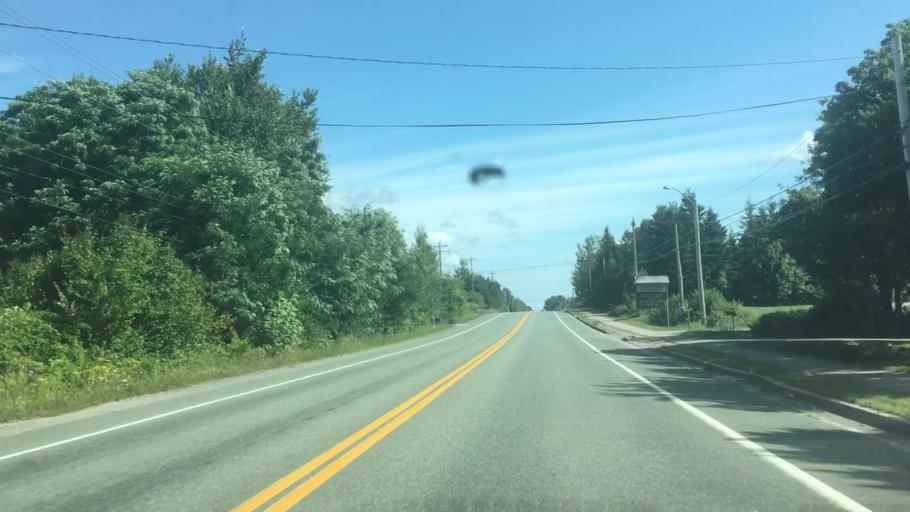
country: CA
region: Nova Scotia
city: Sydney
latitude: 46.0587
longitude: -60.3069
